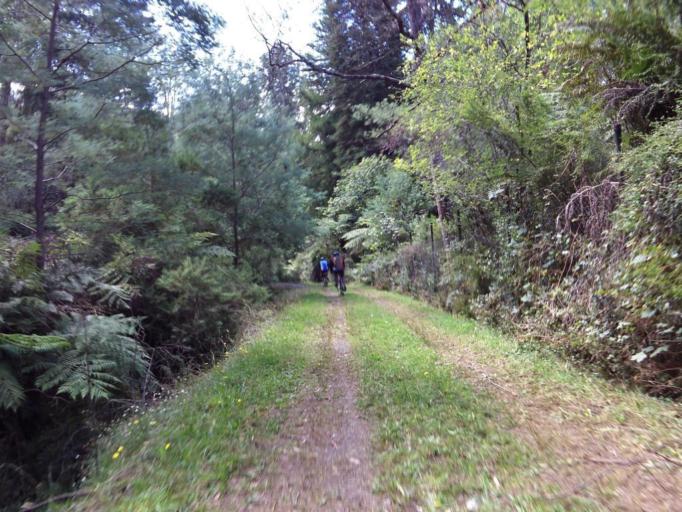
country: AU
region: Victoria
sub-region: Yarra Ranges
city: Millgrove
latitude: -37.7020
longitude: 145.7850
